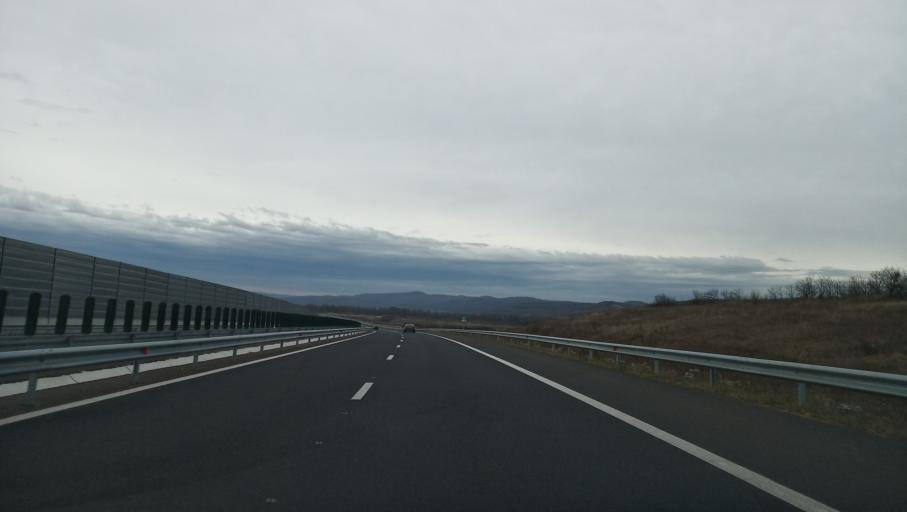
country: RO
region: Hunedoara
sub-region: Comuna Ilia
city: Ilia
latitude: 45.9473
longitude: 22.7148
